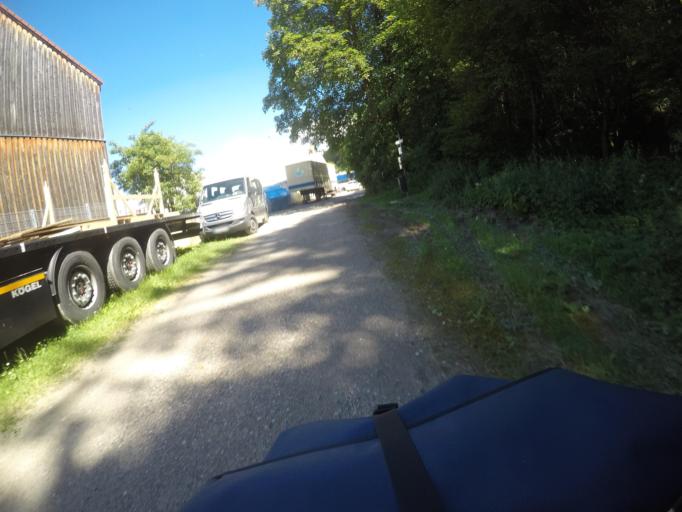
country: DE
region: Bavaria
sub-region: Swabia
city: Fuessen
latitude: 47.5670
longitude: 10.6745
